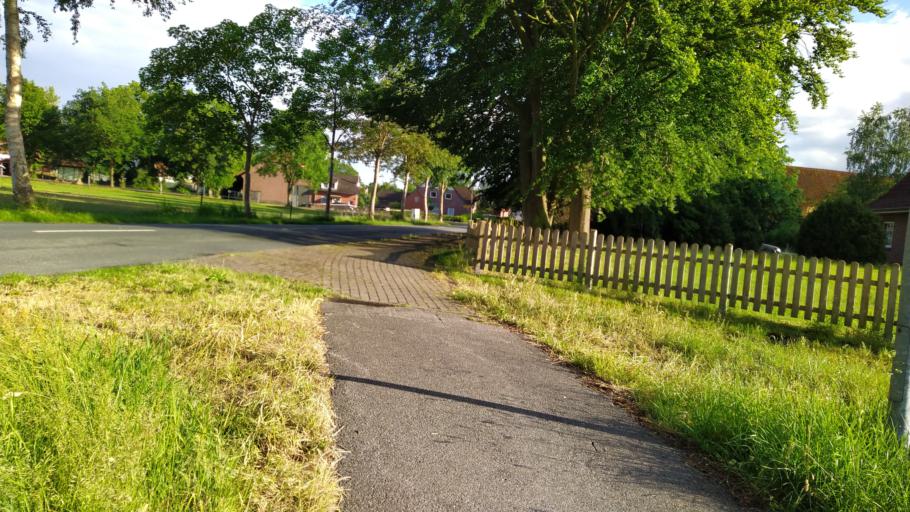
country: DE
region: Lower Saxony
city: Brest
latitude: 53.4520
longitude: 9.3830
